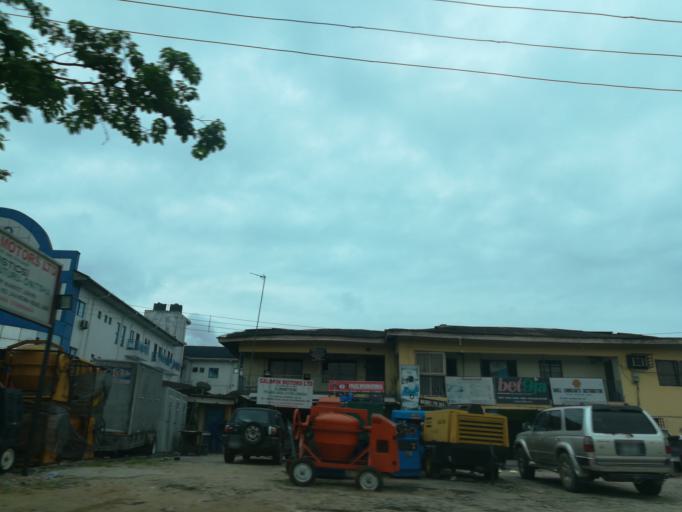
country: NG
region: Rivers
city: Port Harcourt
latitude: 4.8375
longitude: 7.0244
